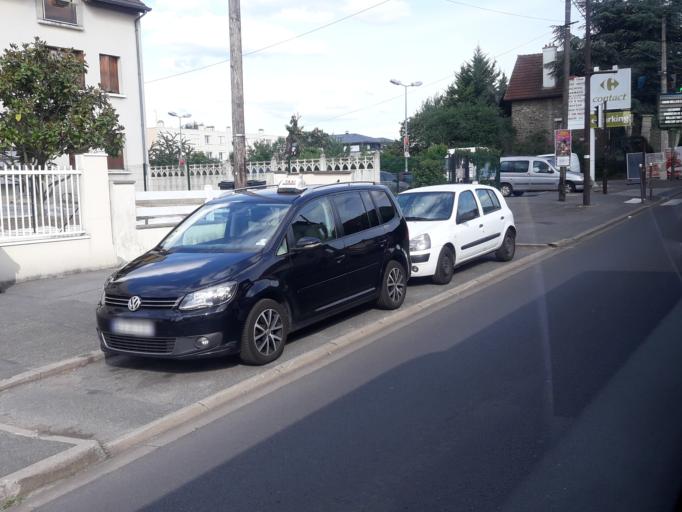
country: FR
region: Ile-de-France
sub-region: Departement de l'Essonne
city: Epinay-sur-Orge
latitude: 48.6788
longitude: 2.3176
